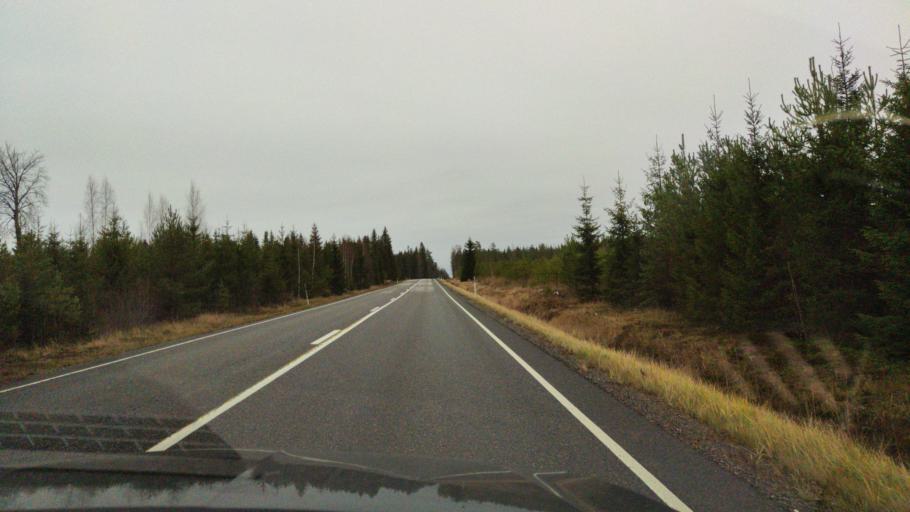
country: FI
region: Varsinais-Suomi
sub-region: Loimaa
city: Ylaene
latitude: 60.7606
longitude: 22.4315
